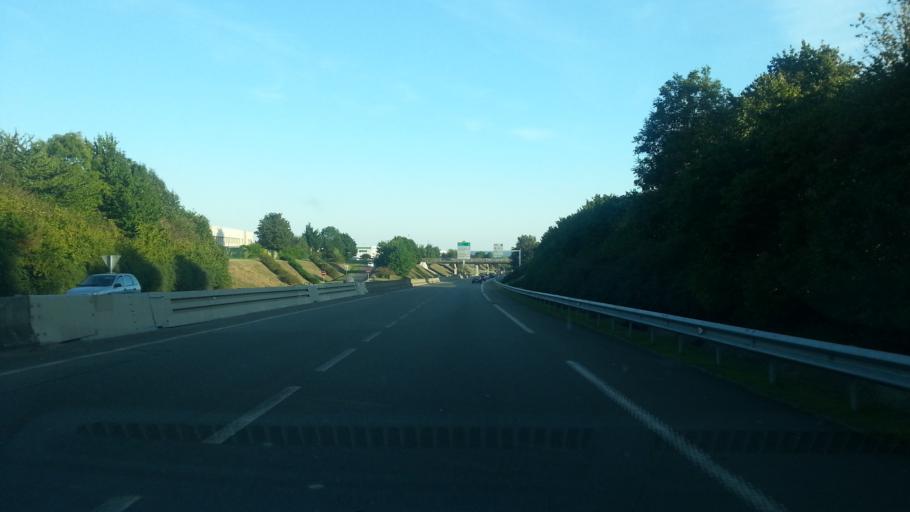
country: FR
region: Picardie
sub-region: Departement de l'Oise
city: Jaux
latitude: 49.4071
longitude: 2.7784
